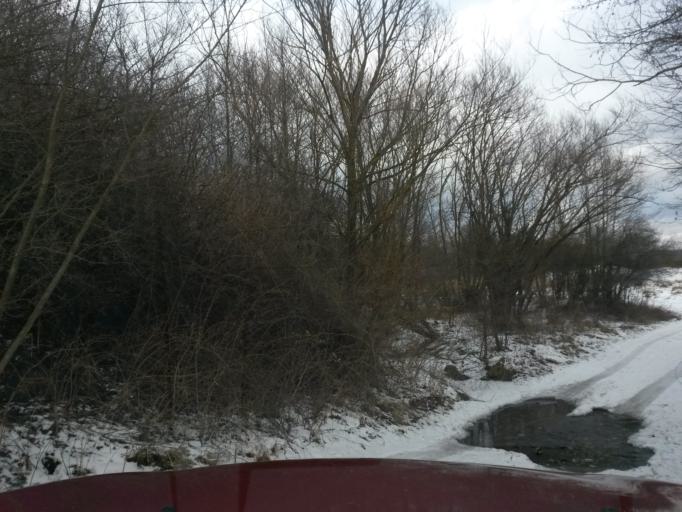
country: SK
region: Kosicky
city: Krompachy
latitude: 48.8159
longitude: 20.8258
